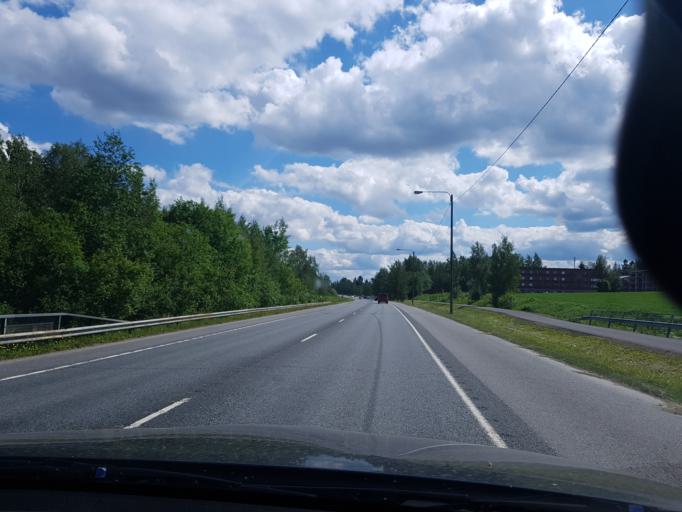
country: FI
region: Haeme
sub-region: Haemeenlinna
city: Parola
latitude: 61.0403
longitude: 24.4028
